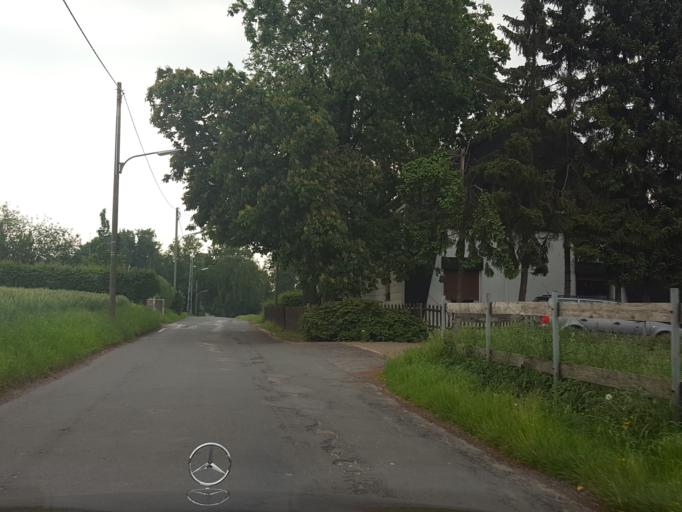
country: DE
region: North Rhine-Westphalia
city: Oer-Erkenschwick
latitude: 51.6176
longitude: 7.2444
